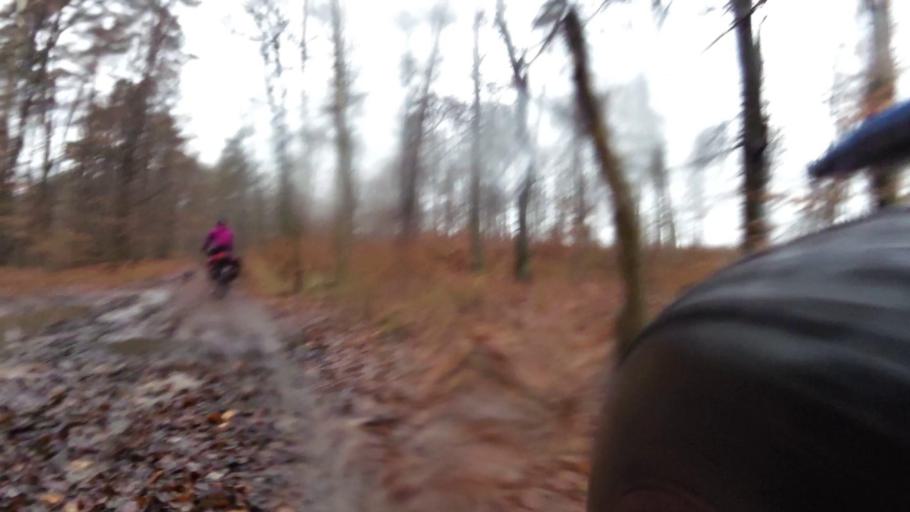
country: PL
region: West Pomeranian Voivodeship
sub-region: Powiat drawski
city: Czaplinek
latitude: 53.5169
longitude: 16.1994
